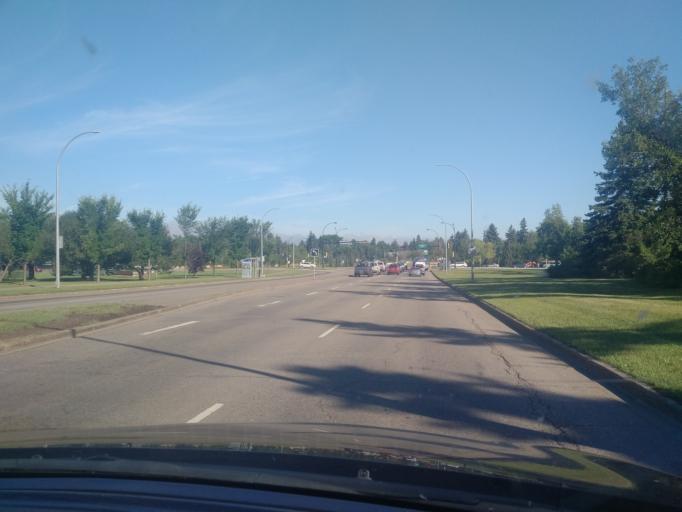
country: CA
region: Alberta
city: Edmonton
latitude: 53.5069
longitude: -113.5233
